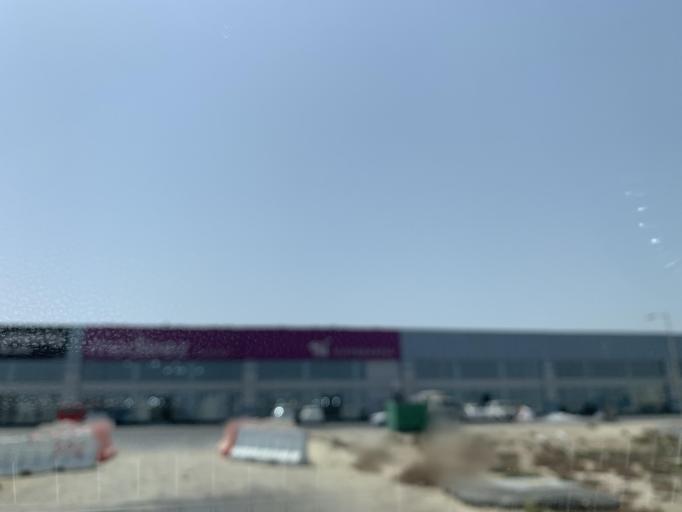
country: BH
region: Northern
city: Madinat `Isa
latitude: 26.1909
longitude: 50.5422
